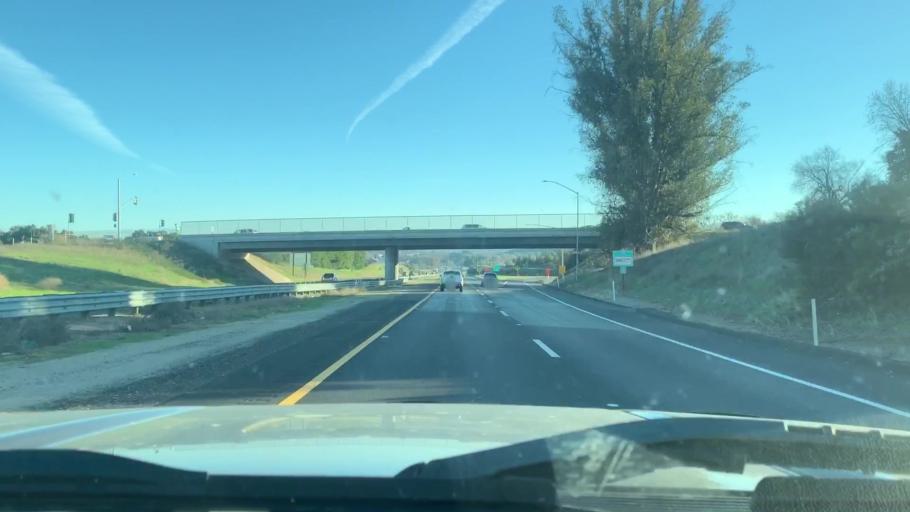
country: US
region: California
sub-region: San Luis Obispo County
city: Templeton
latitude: 35.5446
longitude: -120.7150
